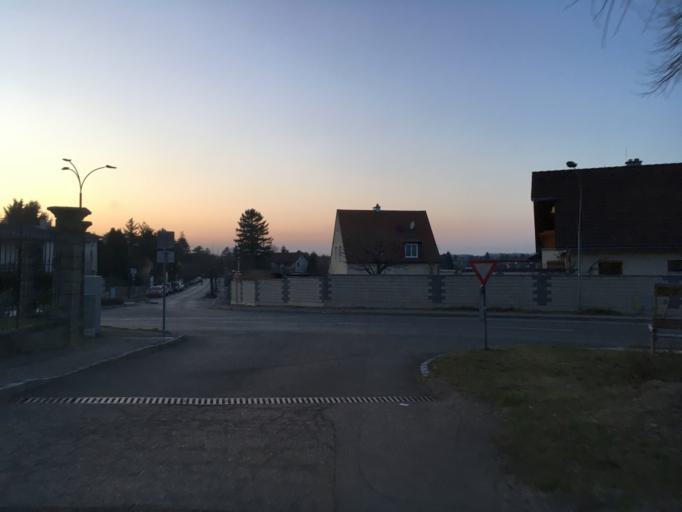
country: AT
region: Lower Austria
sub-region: Politischer Bezirk Tulln
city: Wordern
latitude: 48.3300
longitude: 16.2206
